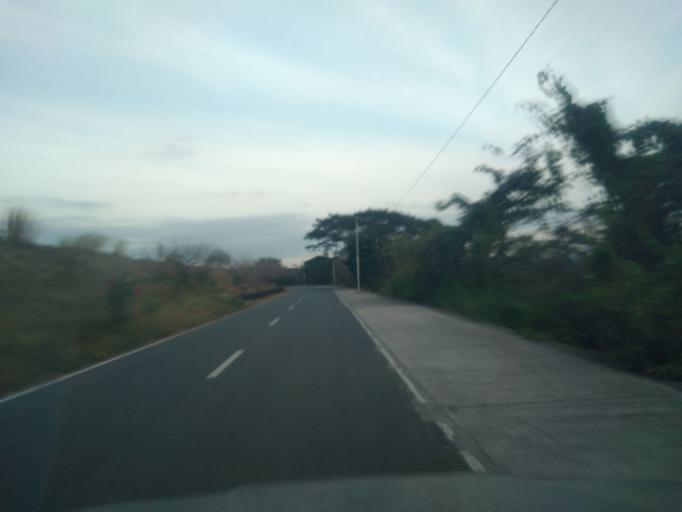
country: PH
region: Central Luzon
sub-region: Province of Pampanga
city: Santa Rita
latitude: 15.0175
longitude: 120.6103
